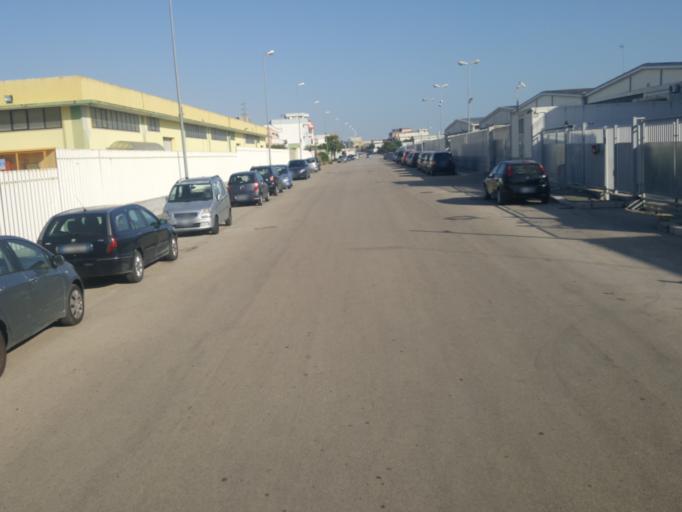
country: IT
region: Apulia
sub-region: Provincia di Barletta - Andria - Trani
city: Barletta
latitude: 41.3080
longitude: 16.3063
